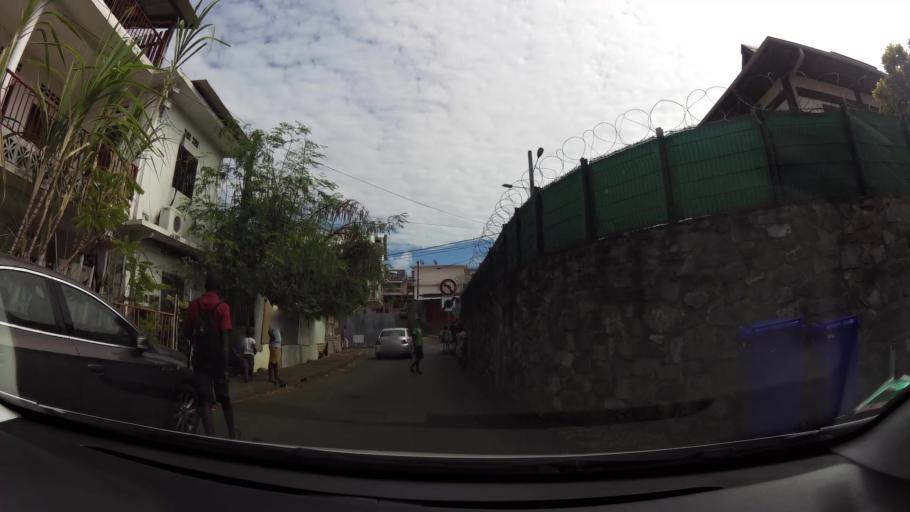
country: YT
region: Mamoudzou
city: Mamoudzou
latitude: -12.7807
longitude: 45.2318
